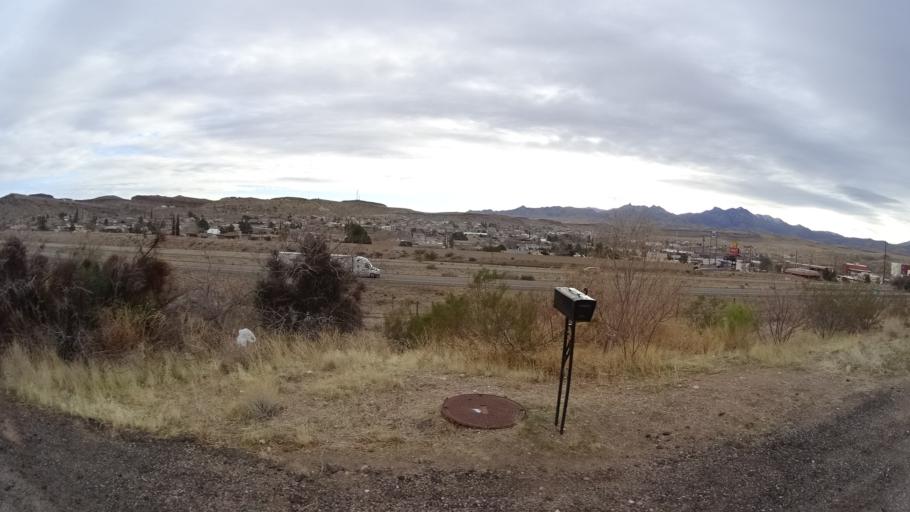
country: US
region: Arizona
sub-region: Mohave County
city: Kingman
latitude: 35.1933
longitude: -114.0682
